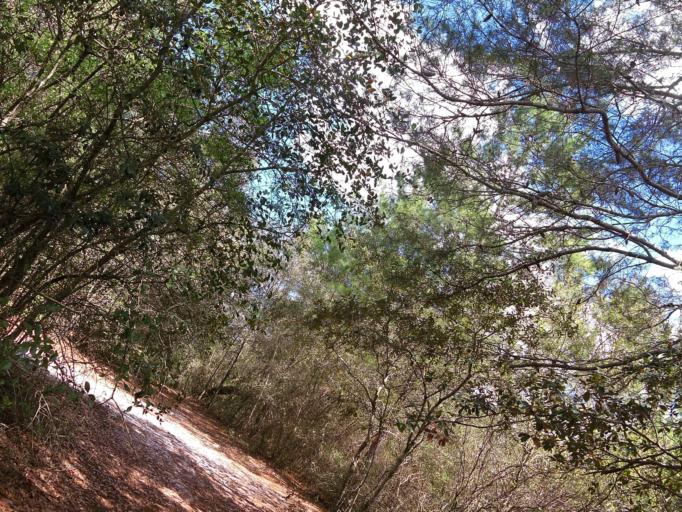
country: US
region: Florida
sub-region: Putnam County
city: Interlachen
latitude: 29.7708
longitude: -81.8678
